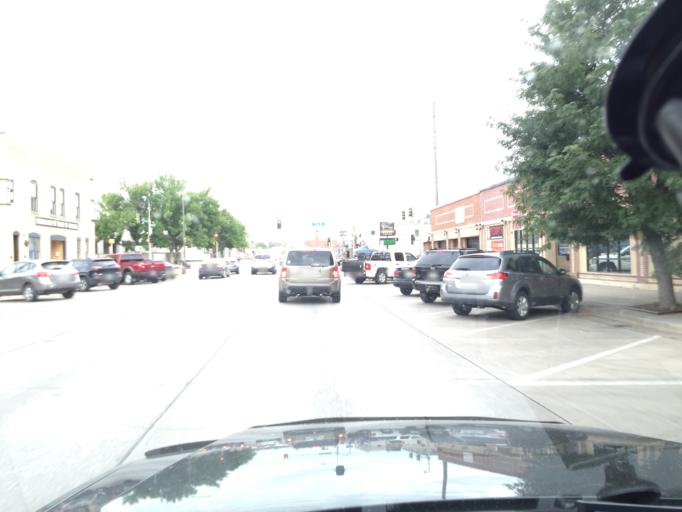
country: US
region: South Dakota
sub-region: Pennington County
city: Rapid City
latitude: 44.0819
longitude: -103.2317
